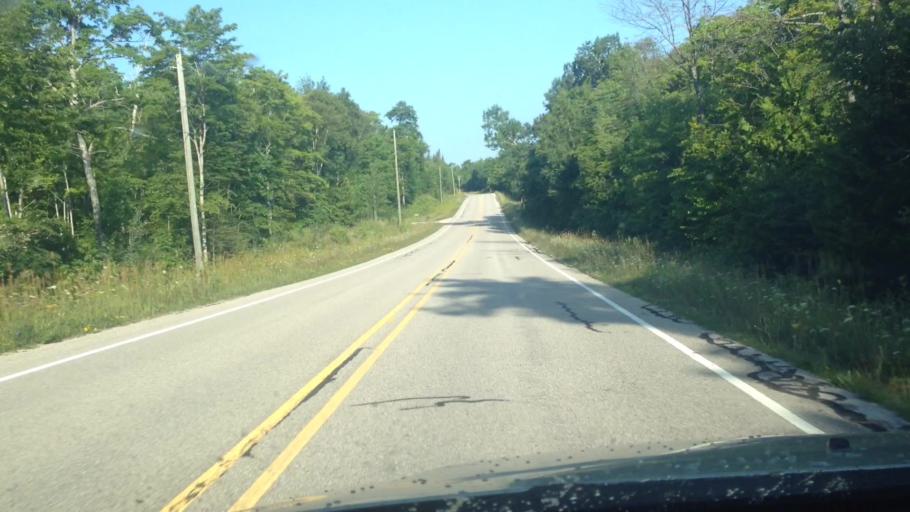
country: US
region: Michigan
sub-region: Mackinac County
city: Saint Ignace
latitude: 45.8933
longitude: -84.8061
